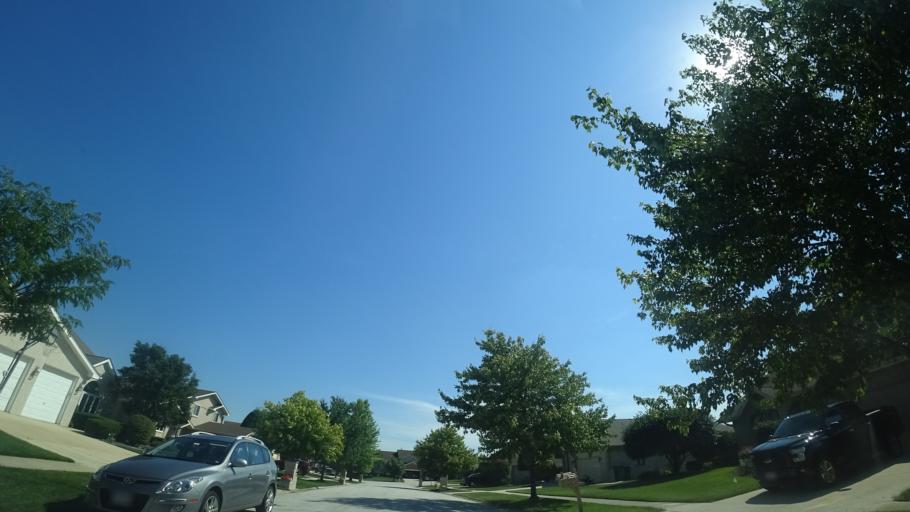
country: US
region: Illinois
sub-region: Will County
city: Mokena
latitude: 41.5655
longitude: -87.9073
